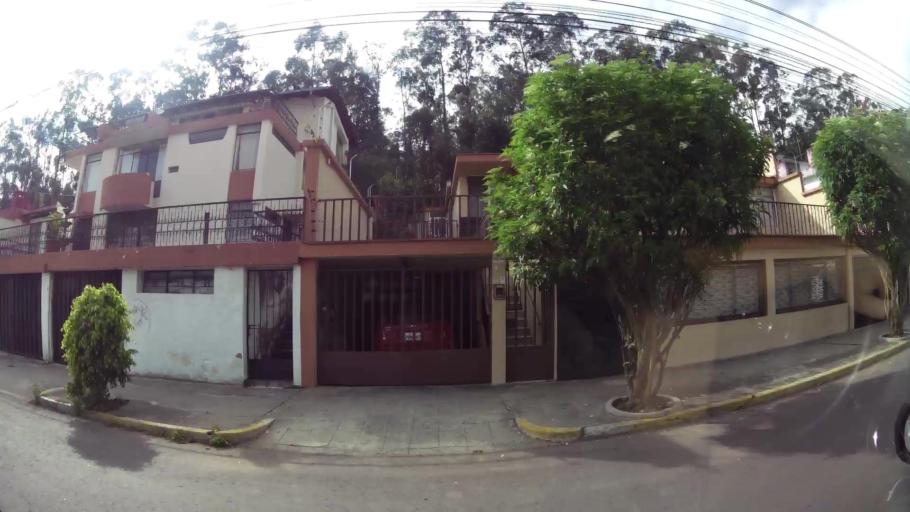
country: EC
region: Pichincha
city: Quito
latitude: -0.1788
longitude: -78.4722
